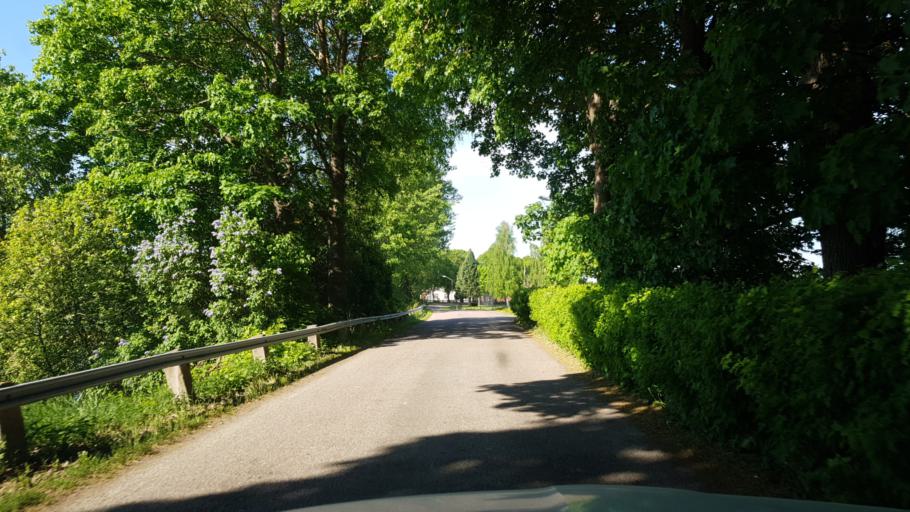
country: SE
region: Dalarna
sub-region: Hedemora Kommun
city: Langshyttan
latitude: 60.4198
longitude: 15.9421
